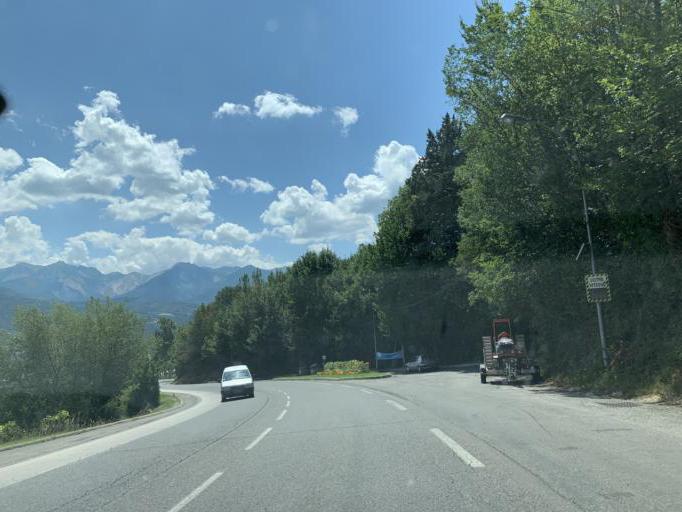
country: FR
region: Provence-Alpes-Cote d'Azur
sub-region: Departement des Hautes-Alpes
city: Embrun
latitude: 44.5590
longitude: 6.4845
